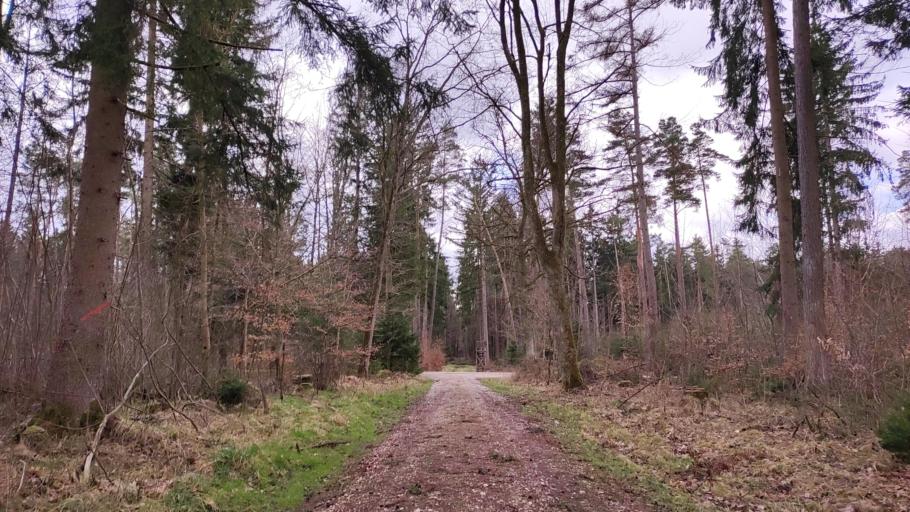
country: DE
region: Bavaria
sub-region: Swabia
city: Landensberg
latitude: 48.4290
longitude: 10.5575
